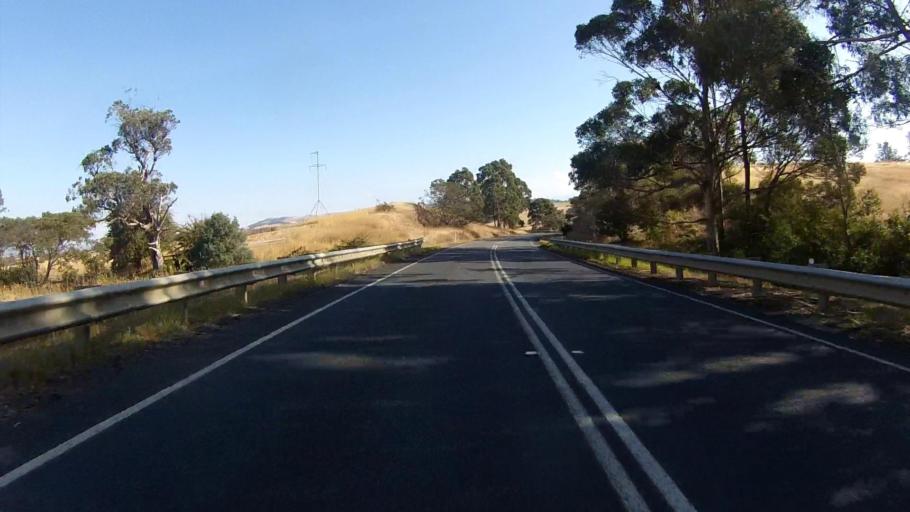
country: AU
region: Tasmania
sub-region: Sorell
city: Sorell
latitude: -42.7009
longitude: 147.5240
